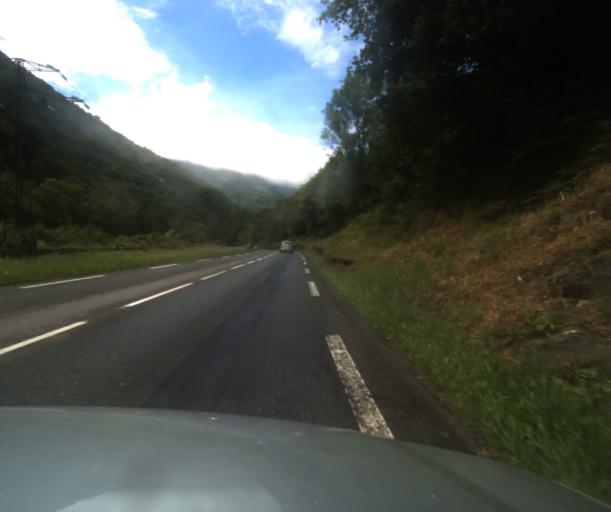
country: FR
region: Midi-Pyrenees
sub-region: Departement des Hautes-Pyrenees
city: Pierrefitte-Nestalas
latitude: 42.9492
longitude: -0.0625
